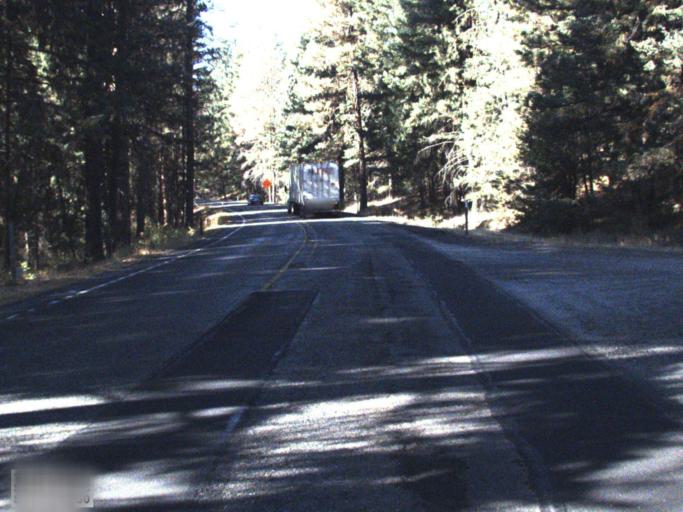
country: US
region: Washington
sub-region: Yakima County
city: Tieton
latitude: 46.6754
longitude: -121.0803
